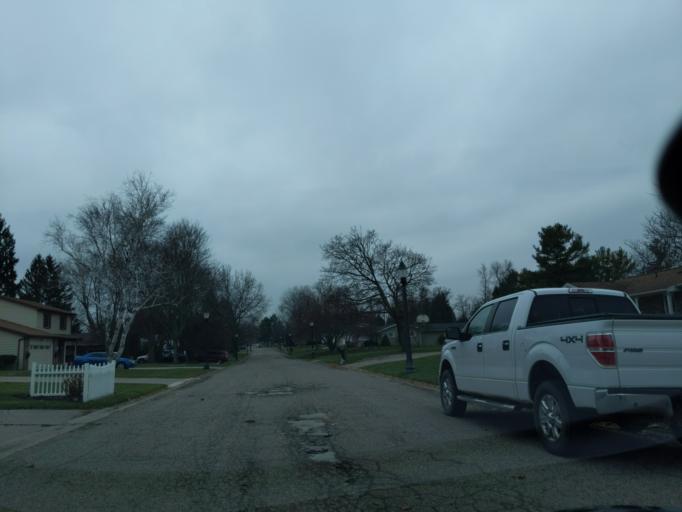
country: US
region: Michigan
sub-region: Eaton County
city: Waverly
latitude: 42.7292
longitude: -84.6318
